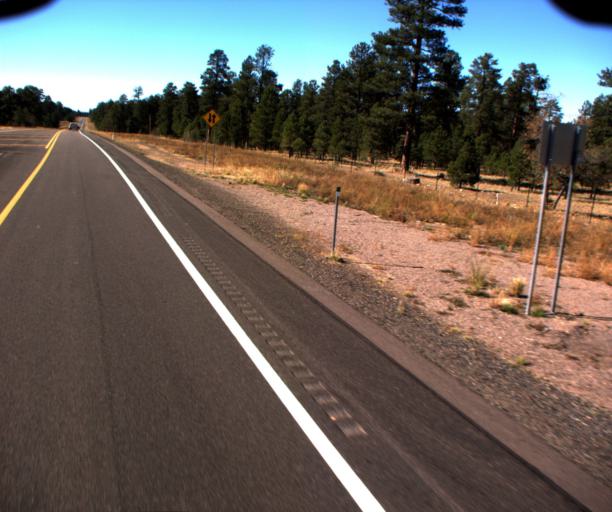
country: US
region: Arizona
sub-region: Apache County
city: Saint Michaels
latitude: 35.6814
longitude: -109.2174
